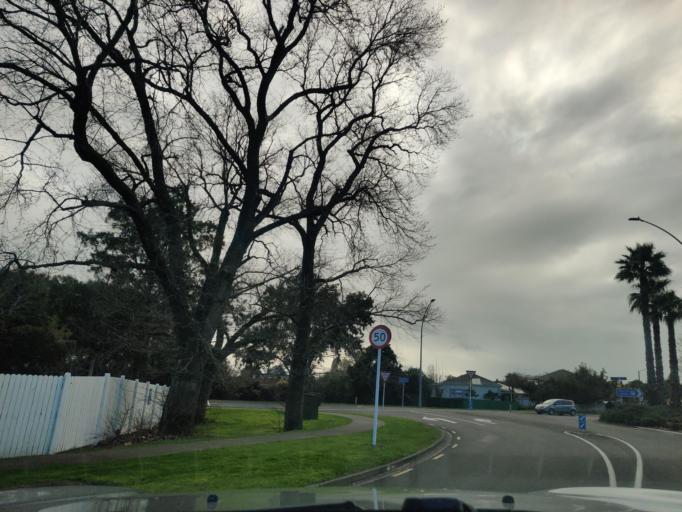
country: NZ
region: Hawke's Bay
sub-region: Hastings District
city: Hastings
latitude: -39.6687
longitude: 176.8813
